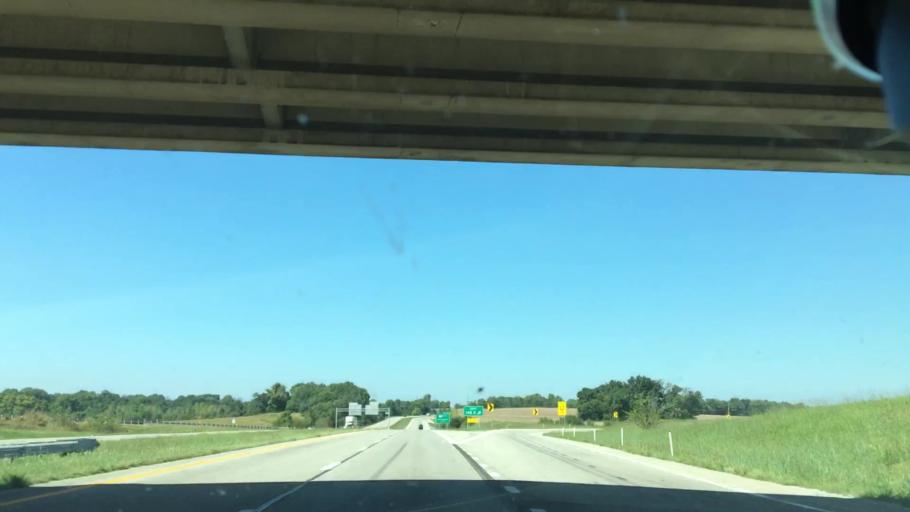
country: US
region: Kentucky
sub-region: Henderson County
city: Henderson
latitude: 37.7973
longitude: -87.5580
